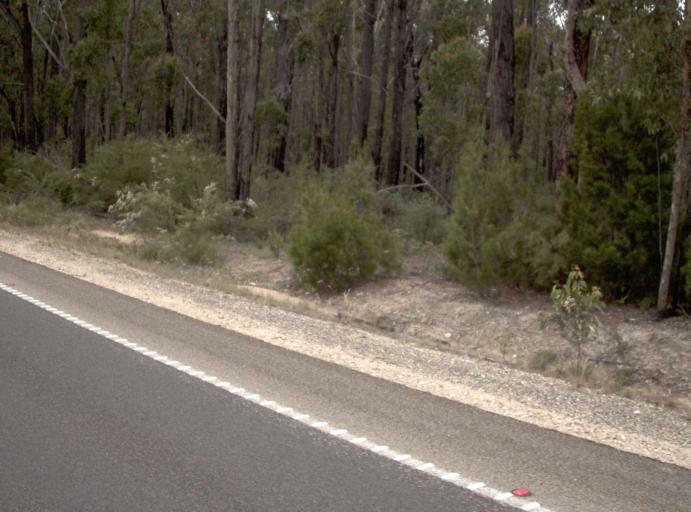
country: AU
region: Victoria
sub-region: East Gippsland
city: Lakes Entrance
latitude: -37.7110
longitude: 147.9842
